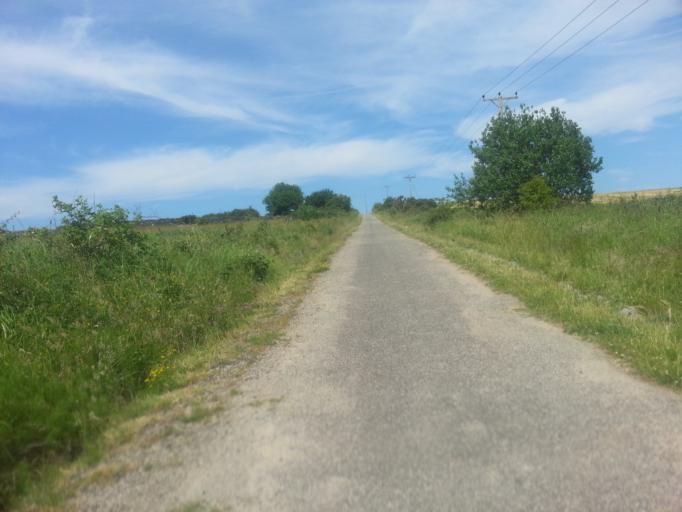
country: GB
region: England
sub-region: County Durham
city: Crook
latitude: 54.7283
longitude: -1.7416
